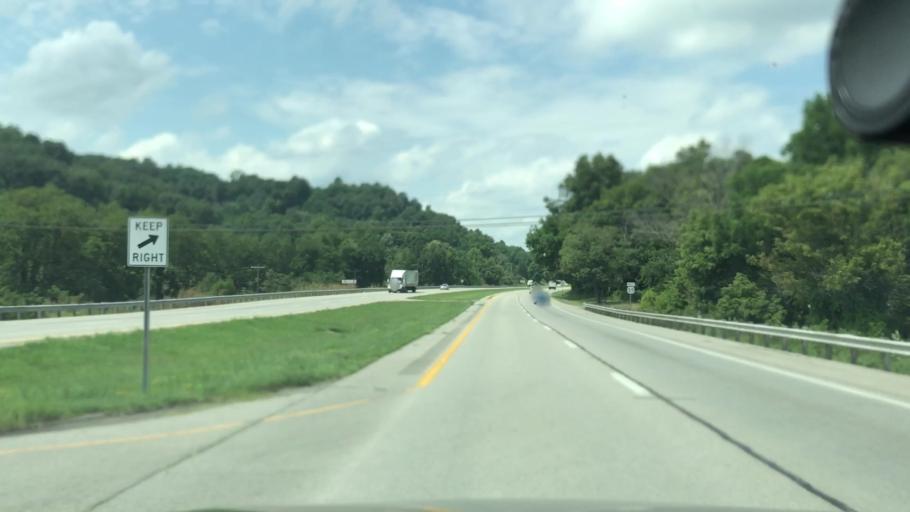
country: US
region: Ohio
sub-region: Jackson County
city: Jackson
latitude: 39.1725
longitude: -82.7460
